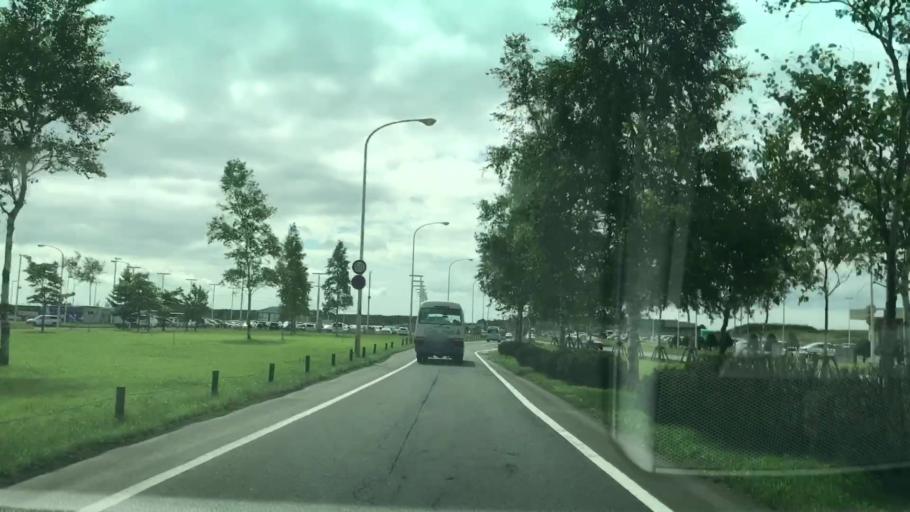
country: JP
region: Hokkaido
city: Chitose
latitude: 42.7825
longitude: 141.6777
